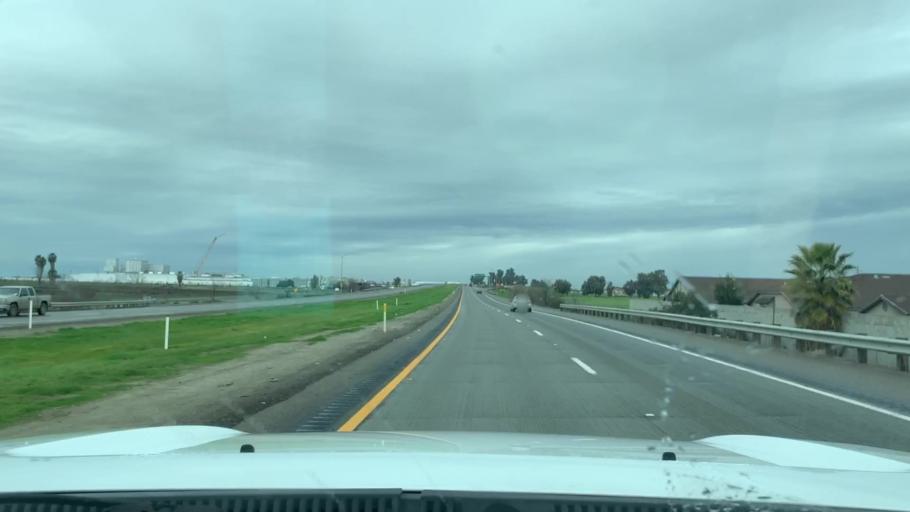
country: US
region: California
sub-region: Kings County
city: Lemoore
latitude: 36.2902
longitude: -119.8083
